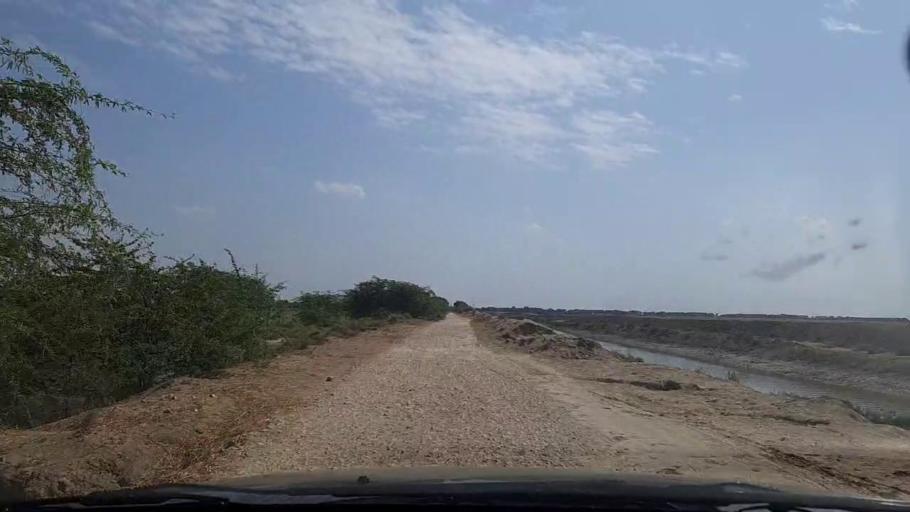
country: PK
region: Sindh
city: Mirpur Batoro
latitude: 24.5733
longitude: 68.1969
